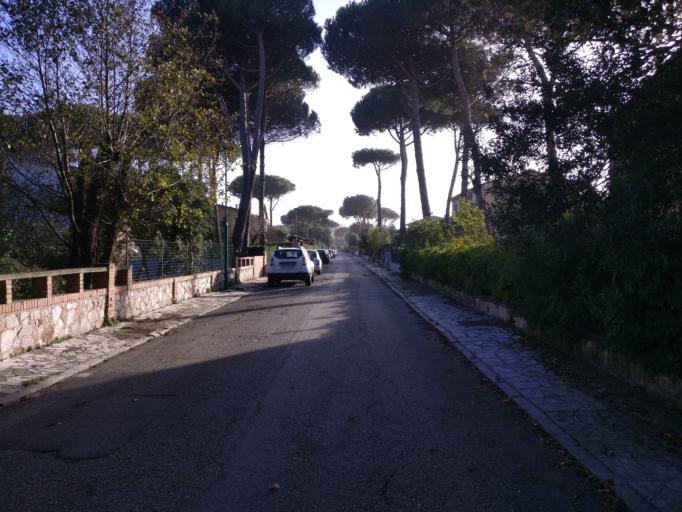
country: IT
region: Tuscany
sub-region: Province of Pisa
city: Marina di Pisa-Tirrenia-Calambrone
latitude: 43.6129
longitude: 10.2932
